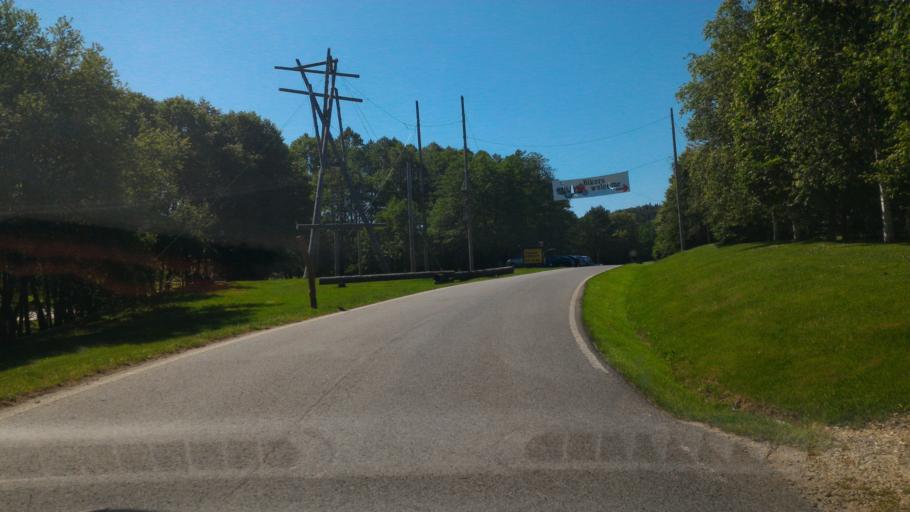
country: DE
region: Saxony
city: Kurort Oybin
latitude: 50.7986
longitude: 14.7140
